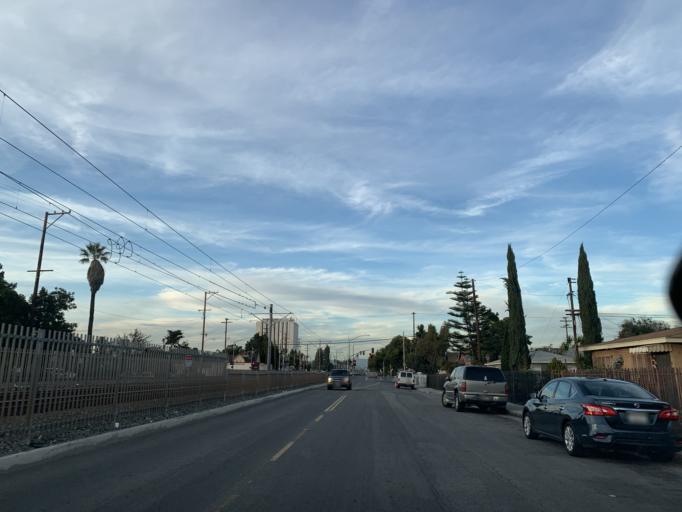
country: US
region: California
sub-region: Los Angeles County
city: Compton
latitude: 33.8872
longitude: -118.2235
